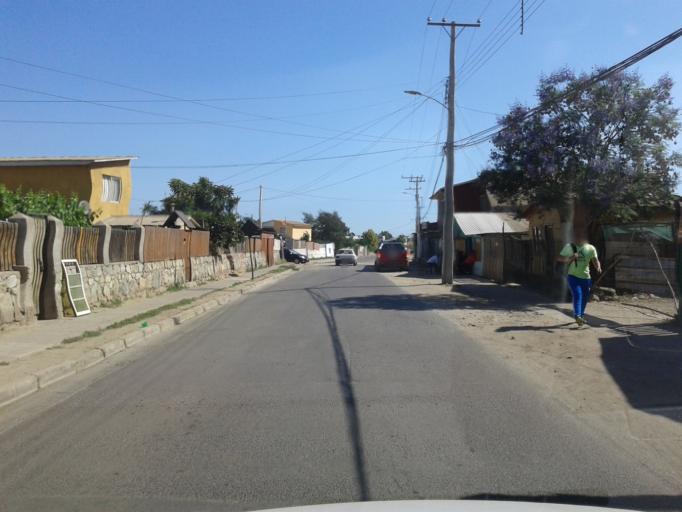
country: CL
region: Valparaiso
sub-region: Provincia de Quillota
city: Quillota
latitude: -32.8753
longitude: -71.2578
